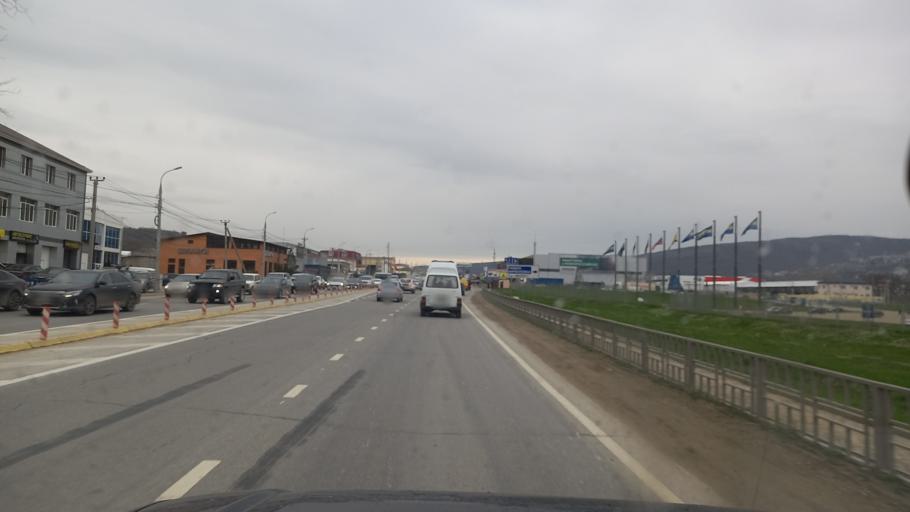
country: RU
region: Krasnodarskiy
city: Gayduk
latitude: 44.7703
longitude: 37.6979
